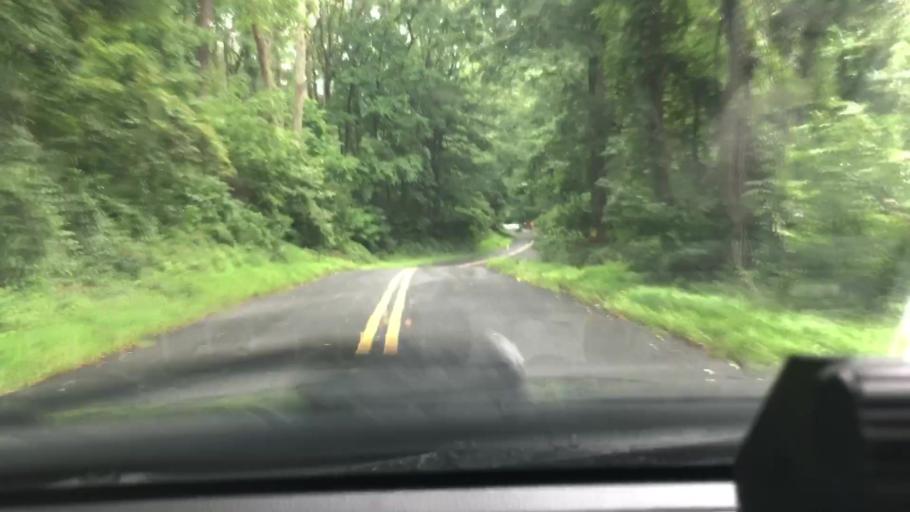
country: US
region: Pennsylvania
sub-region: Lehigh County
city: Macungie
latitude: 40.4785
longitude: -75.5499
